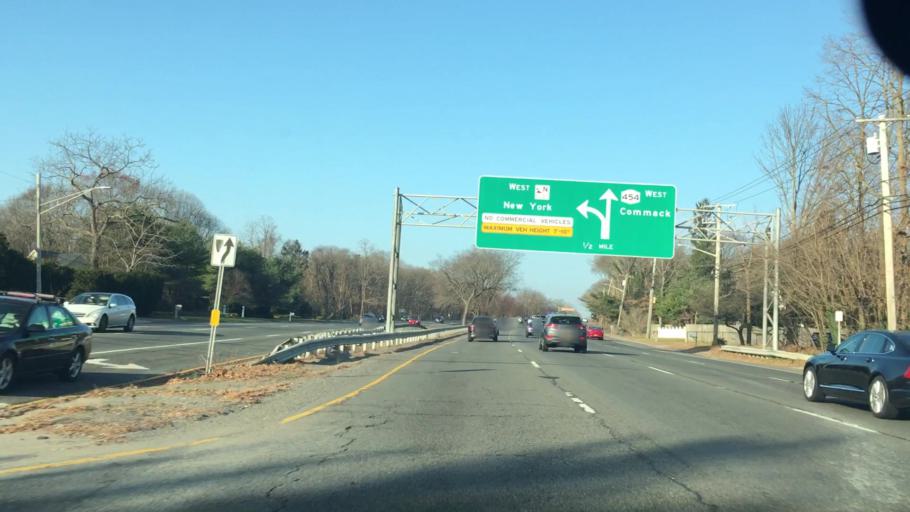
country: US
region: New York
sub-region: Suffolk County
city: Hauppauge
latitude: 40.8257
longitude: -73.2376
